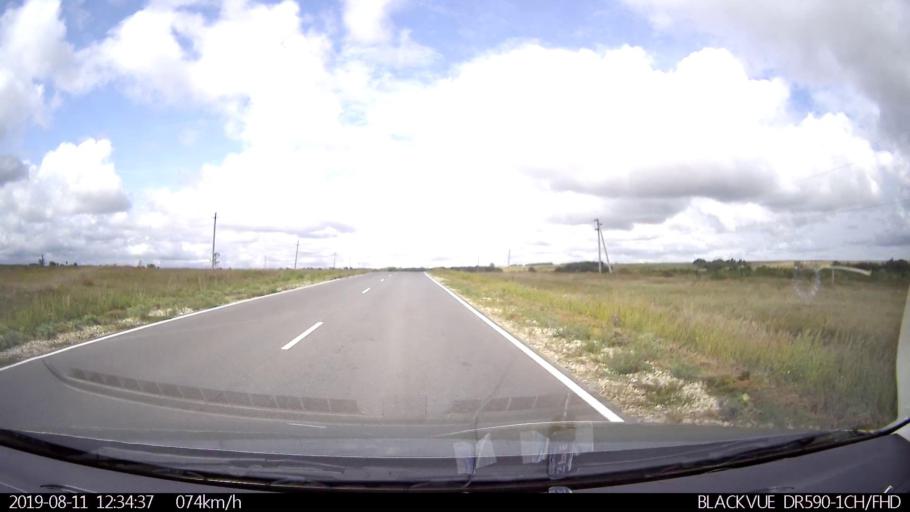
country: RU
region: Ulyanovsk
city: Ignatovka
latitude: 53.8182
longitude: 47.8403
